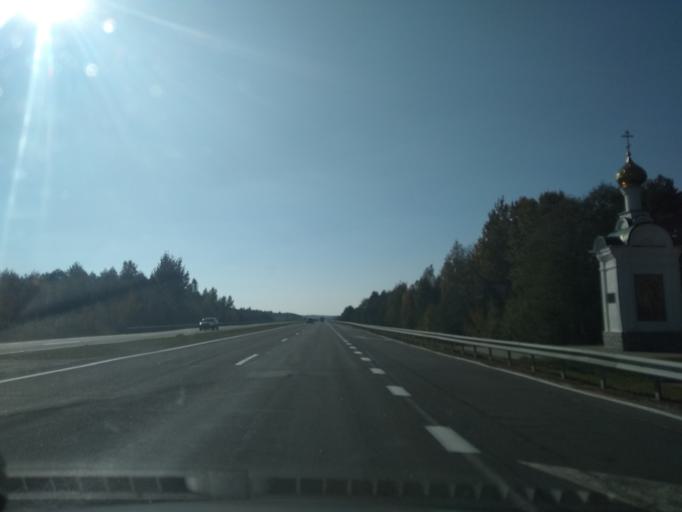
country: BY
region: Brest
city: Ivatsevichy
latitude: 52.7924
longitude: 25.5609
